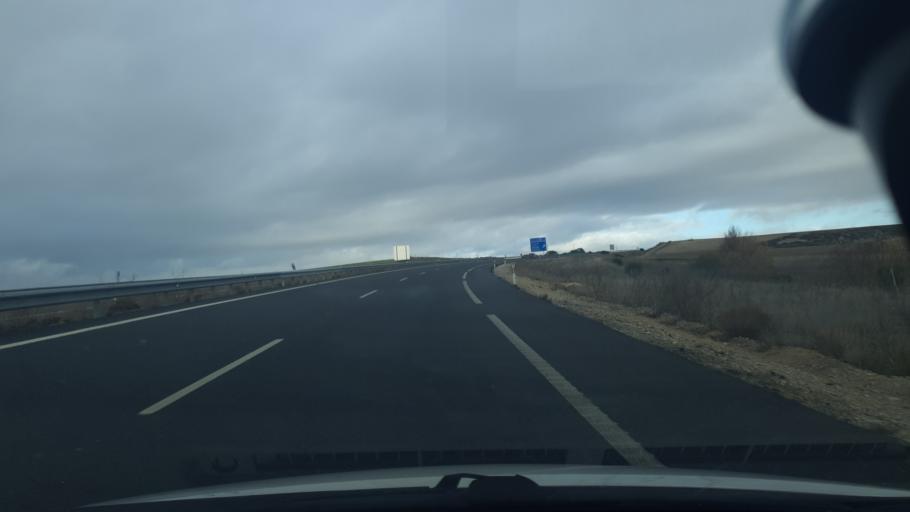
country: ES
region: Castille and Leon
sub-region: Provincia de Segovia
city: Cuellar
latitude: 41.3968
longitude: -4.2927
